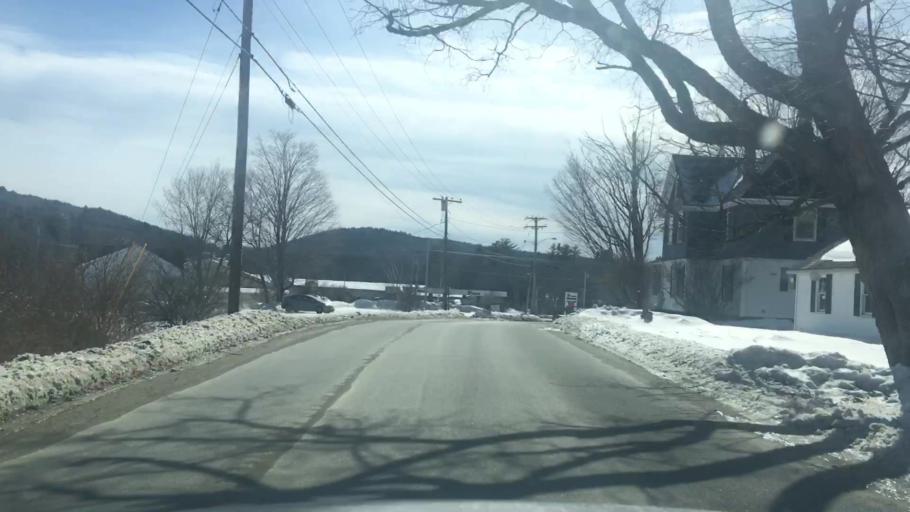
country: US
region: Maine
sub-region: Penobscot County
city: Holden
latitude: 44.7384
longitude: -68.6285
